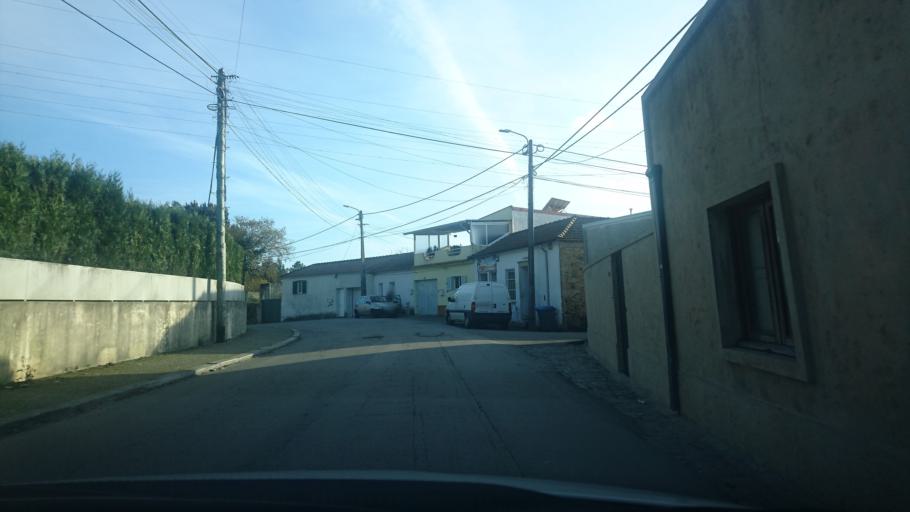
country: PT
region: Aveiro
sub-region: Santa Maria da Feira
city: Nogueira da Regedoura
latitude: 41.0037
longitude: -8.6059
